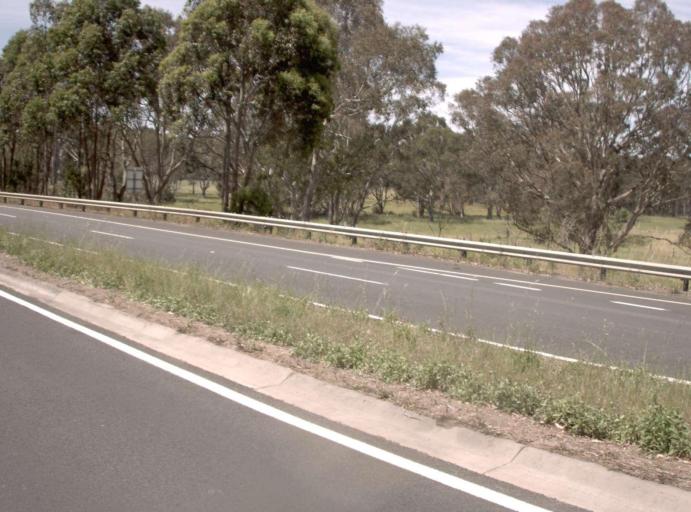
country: AU
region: Victoria
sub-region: Wellington
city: Heyfield
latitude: -38.1486
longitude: 146.7902
